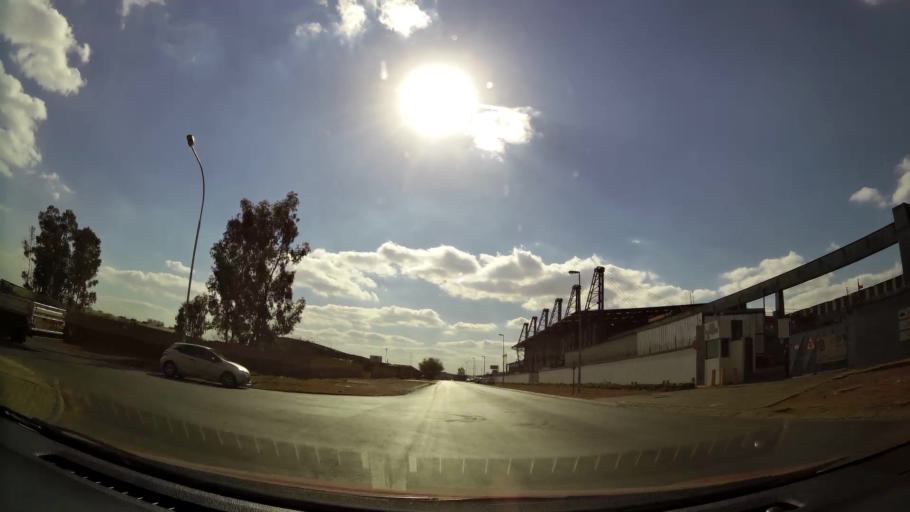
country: ZA
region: Gauteng
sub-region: Ekurhuleni Metropolitan Municipality
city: Tembisa
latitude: -25.9650
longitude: 28.2320
